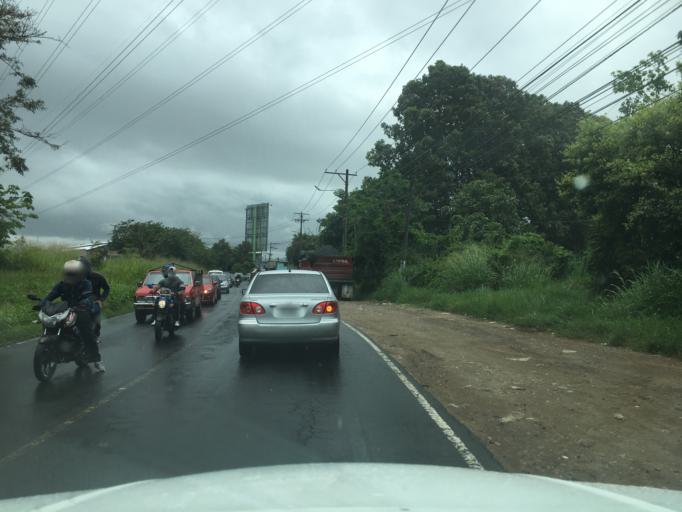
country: GT
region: Guatemala
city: Petapa
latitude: 14.5350
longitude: -90.5294
